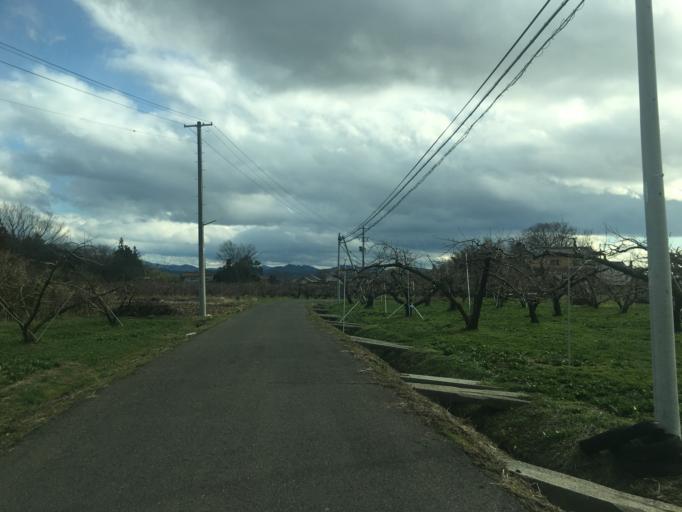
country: JP
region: Fukushima
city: Yanagawamachi-saiwaicho
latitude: 37.8846
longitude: 140.5762
